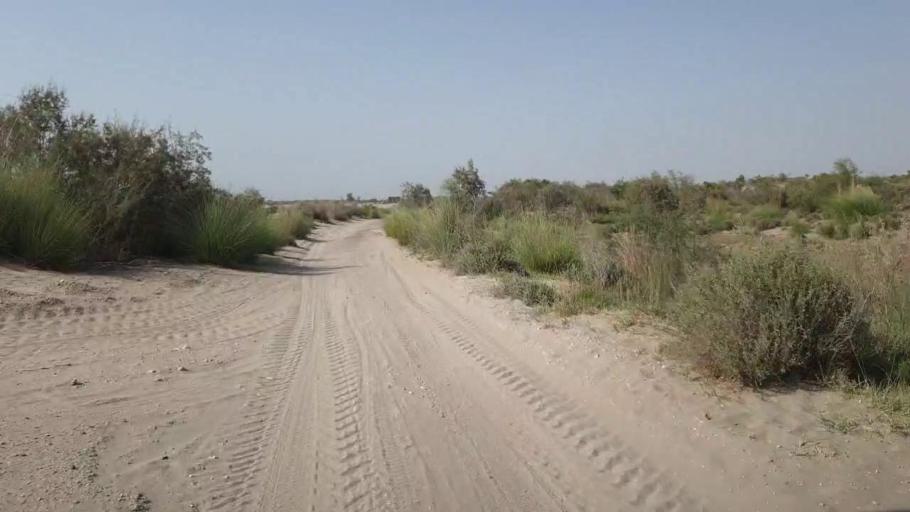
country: PK
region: Sindh
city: Jam Sahib
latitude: 26.5965
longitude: 68.9232
